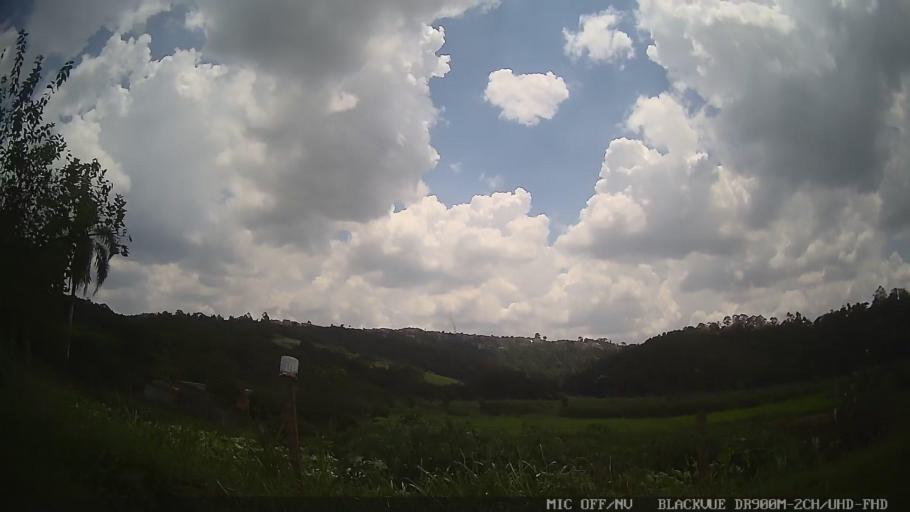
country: BR
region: Sao Paulo
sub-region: Ferraz De Vasconcelos
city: Ferraz de Vasconcelos
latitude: -23.5917
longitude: -46.3642
